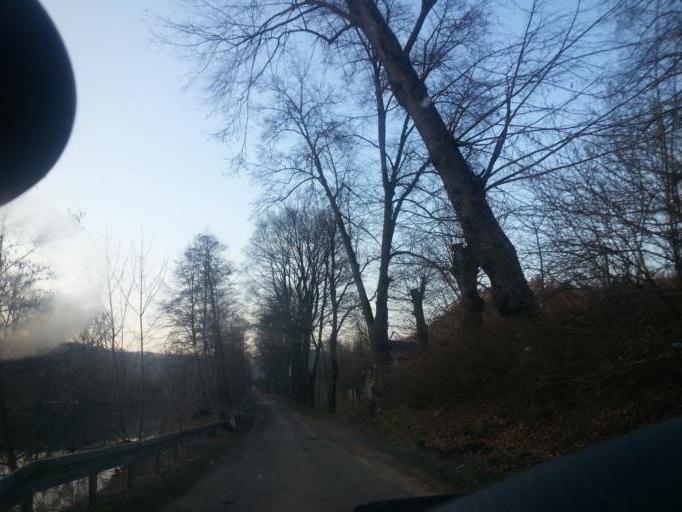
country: PL
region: Lower Silesian Voivodeship
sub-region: Powiat lwowecki
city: Wlen
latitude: 50.9699
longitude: 15.6434
